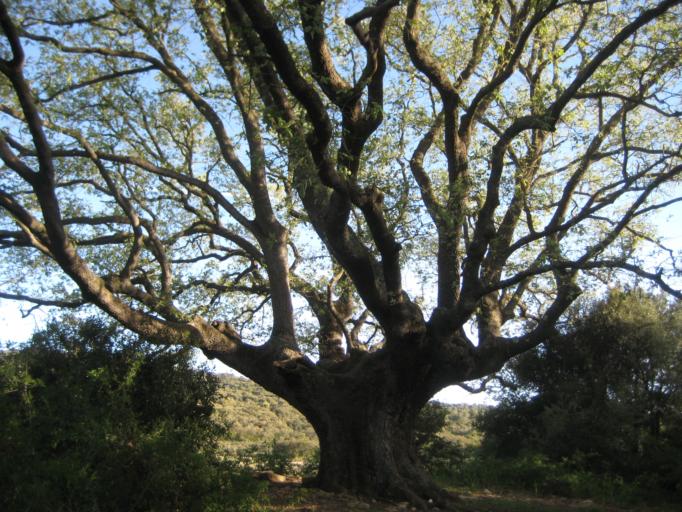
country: ES
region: Catalonia
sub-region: Provincia de Barcelona
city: Bellprat
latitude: 41.4477
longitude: 1.4919
